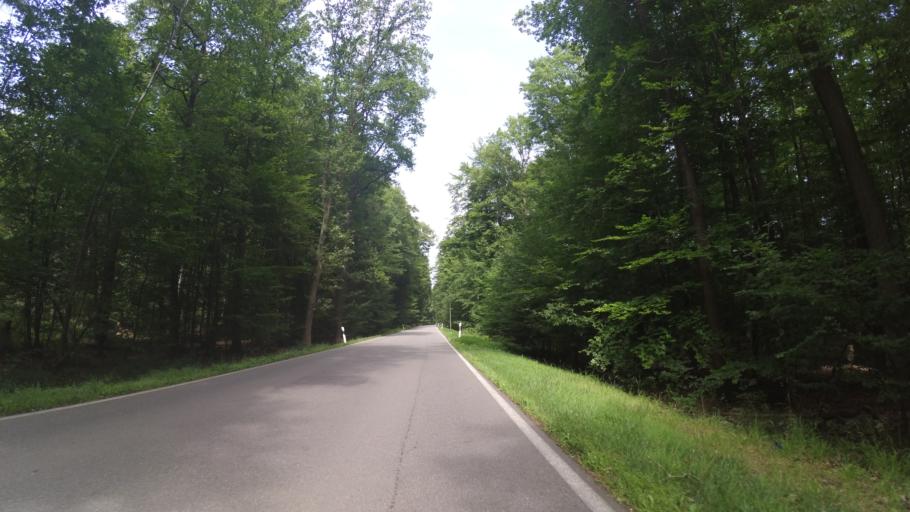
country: DE
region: Rheinland-Pfalz
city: Waldmohr
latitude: 49.3748
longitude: 7.3335
